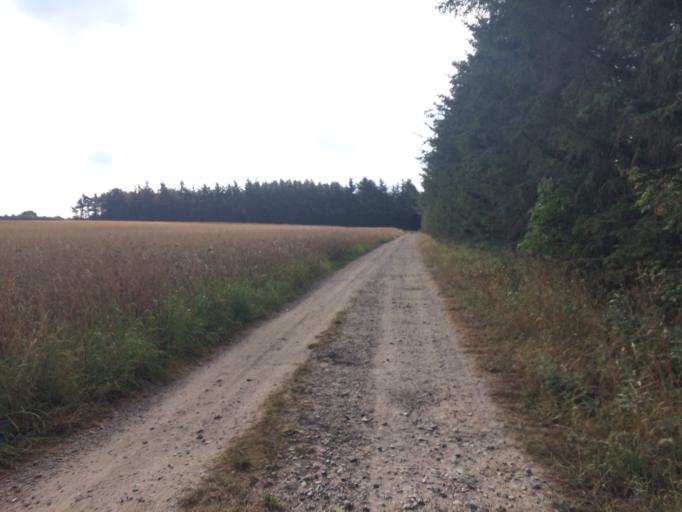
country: DK
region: Central Jutland
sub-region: Holstebro Kommune
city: Vinderup
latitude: 56.6177
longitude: 8.7187
